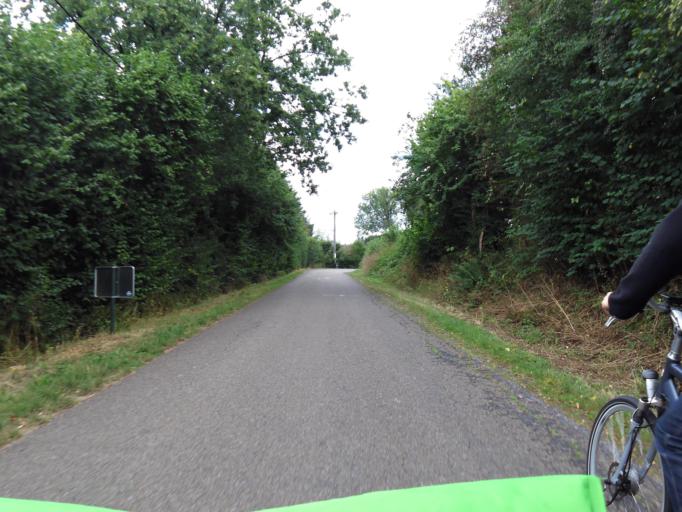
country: BE
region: Wallonia
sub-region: Province de Namur
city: Bievre
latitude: 49.8946
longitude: 5.0078
